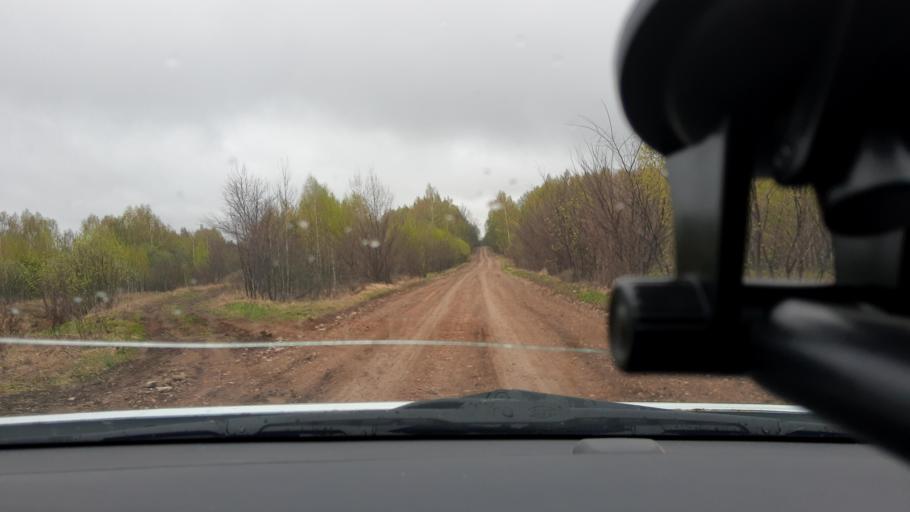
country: RU
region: Bashkortostan
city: Pavlovka
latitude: 55.4359
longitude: 56.3598
